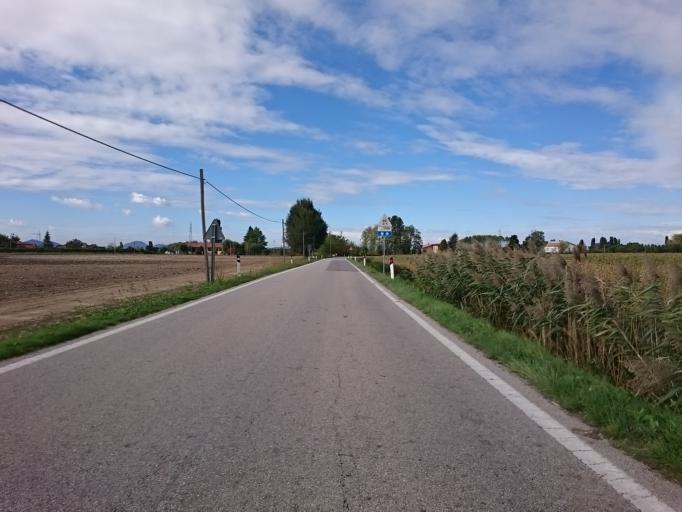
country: IT
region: Veneto
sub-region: Provincia di Padova
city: Bovolenta
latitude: 45.2502
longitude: 11.9398
